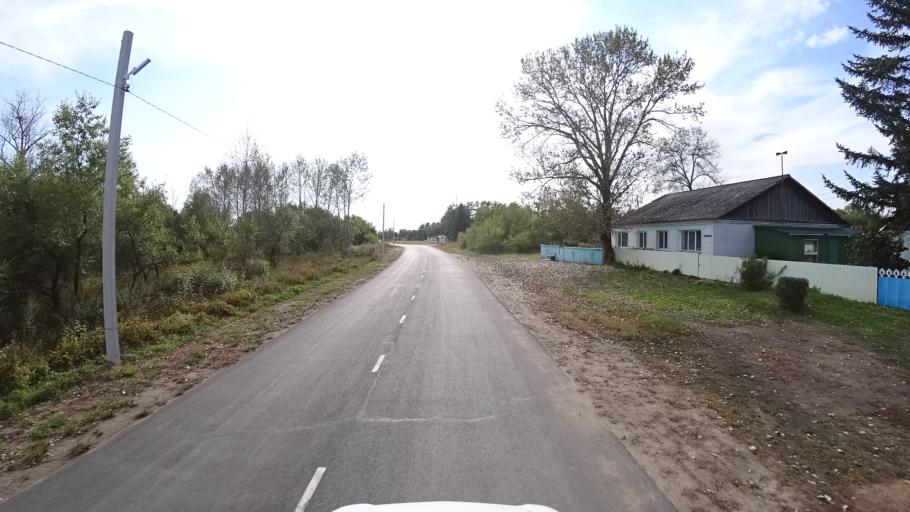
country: RU
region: Amur
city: Arkhara
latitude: 49.3647
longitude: 130.1252
